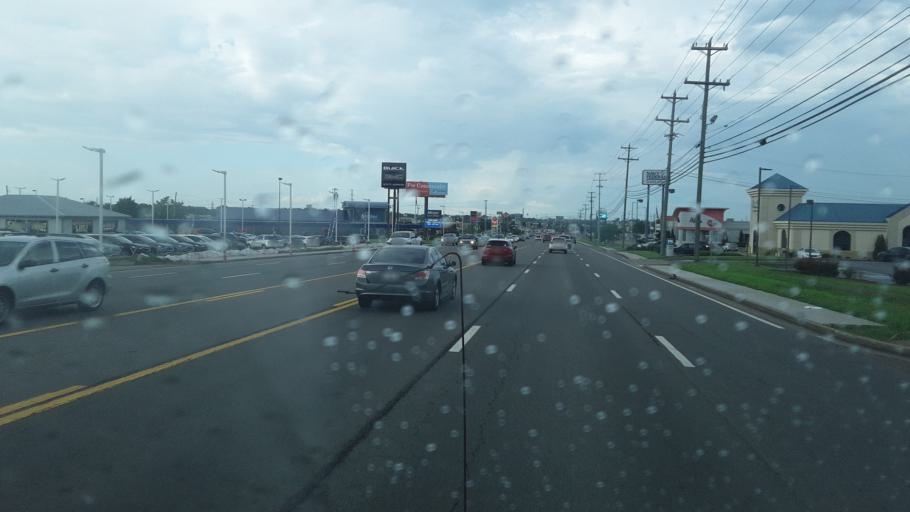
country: US
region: Tennessee
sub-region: Montgomery County
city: Clarksville
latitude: 36.5796
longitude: -87.2990
